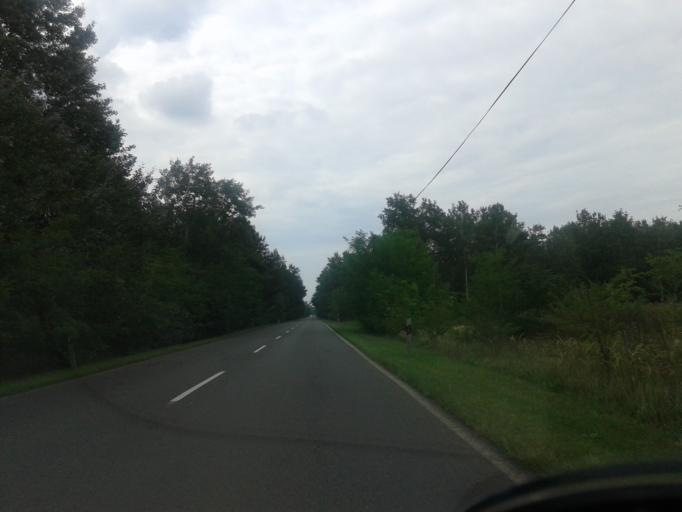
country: HU
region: Csongrad
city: Asotthalom
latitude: 46.2198
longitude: 19.7740
